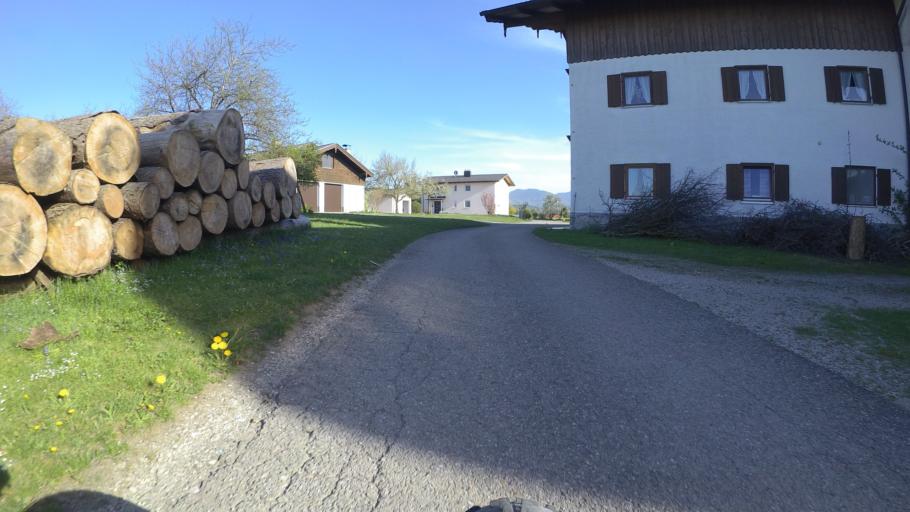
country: DE
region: Bavaria
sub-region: Upper Bavaria
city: Grabenstatt
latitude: 47.8582
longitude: 12.5380
